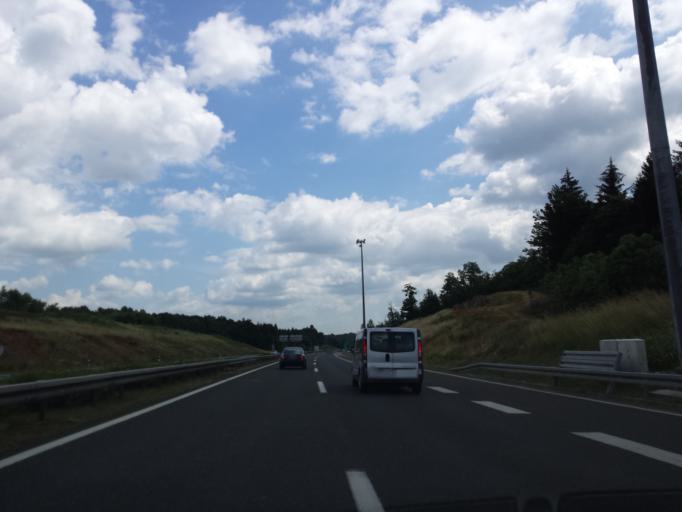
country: HR
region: Karlovacka
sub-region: Grad Ogulin
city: Ogulin
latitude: 45.4213
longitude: 15.2952
